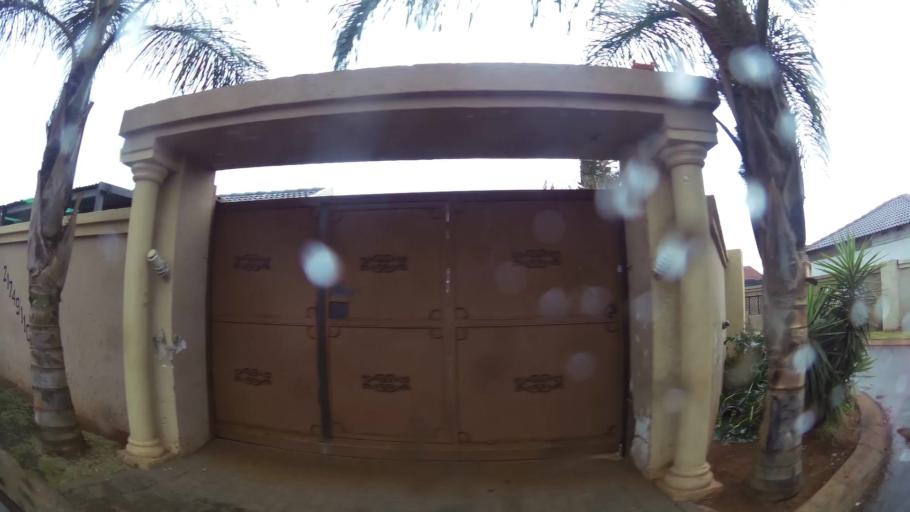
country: ZA
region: Gauteng
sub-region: Ekurhuleni Metropolitan Municipality
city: Germiston
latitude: -26.3312
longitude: 28.2038
